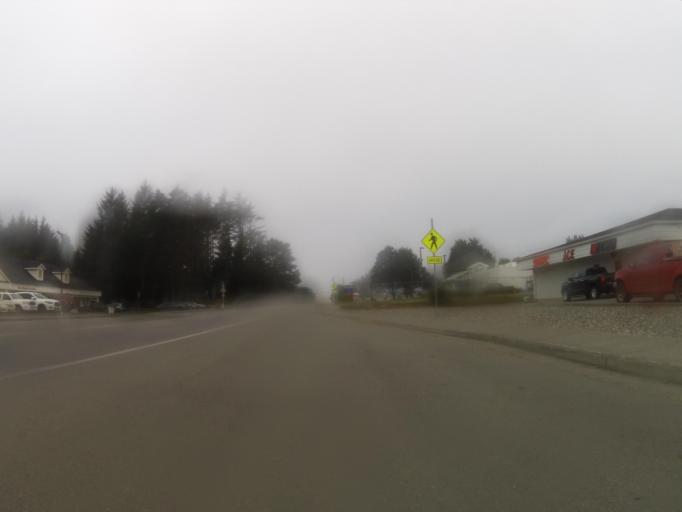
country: US
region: California
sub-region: Del Norte County
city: Crescent City
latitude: 41.7728
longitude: -124.1928
